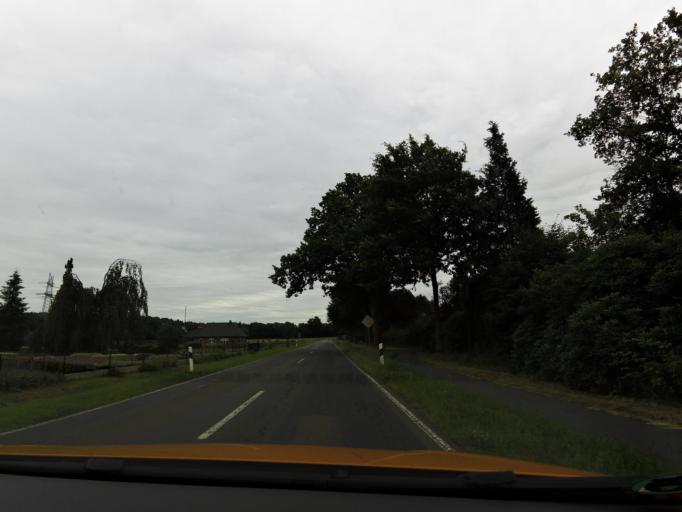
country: DE
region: Lower Saxony
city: Wiefelstede
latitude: 53.2110
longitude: 8.0798
